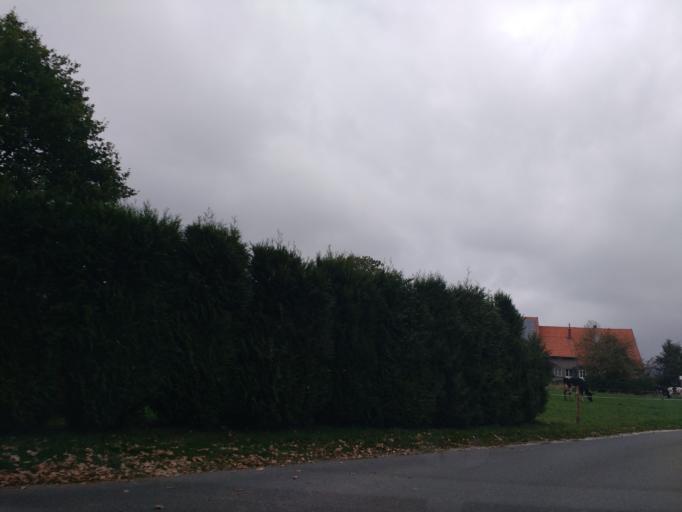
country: DE
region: North Rhine-Westphalia
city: Borgholzhausen
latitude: 52.0859
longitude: 8.2516
